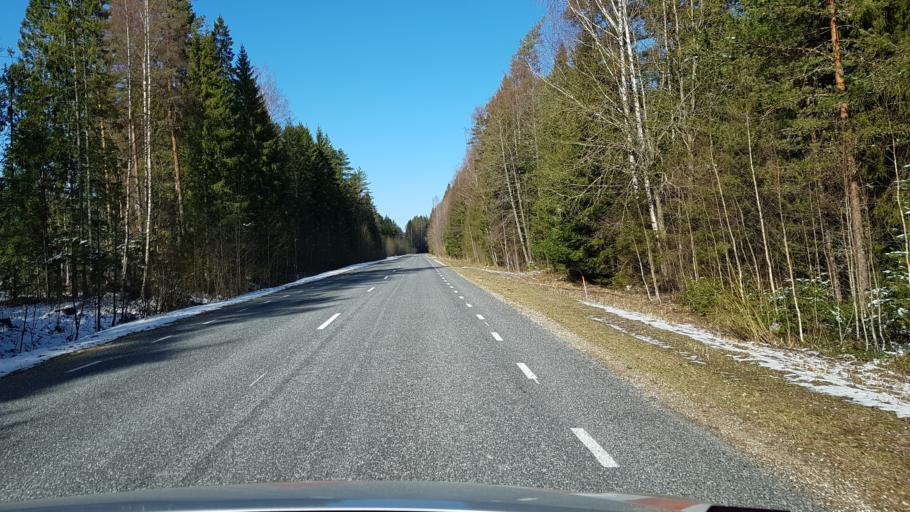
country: EE
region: Harju
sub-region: Loksa linn
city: Loksa
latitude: 59.5640
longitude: 25.9537
